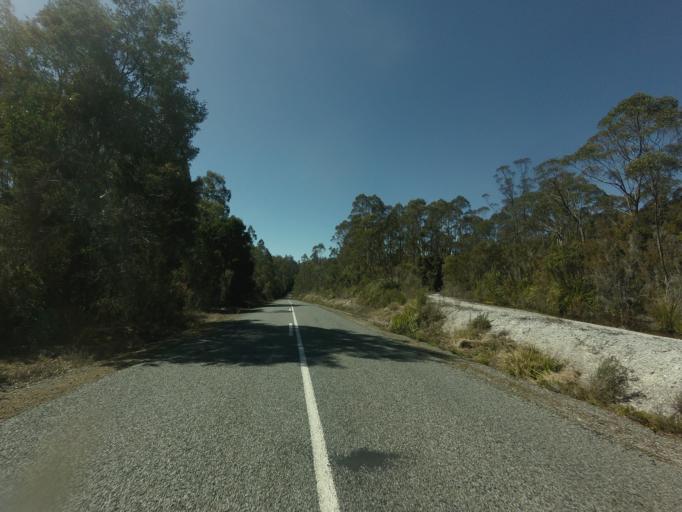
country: AU
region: Tasmania
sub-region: Derwent Valley
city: New Norfolk
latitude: -42.7548
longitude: 146.4100
